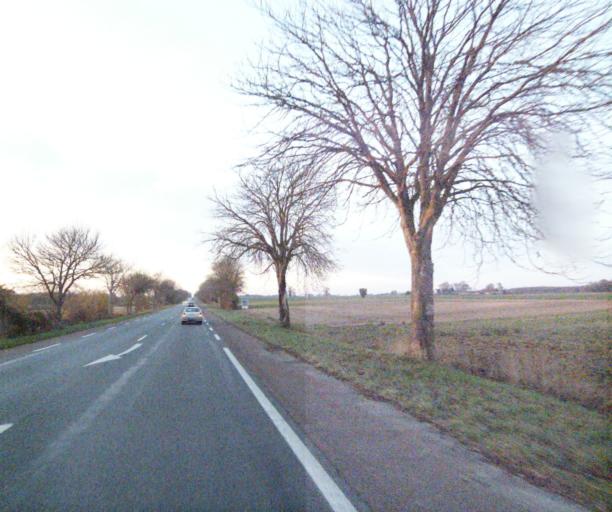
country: FR
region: Poitou-Charentes
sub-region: Departement de la Charente-Maritime
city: Saint-Georges-des-Coteaux
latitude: 45.7948
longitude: -0.7335
